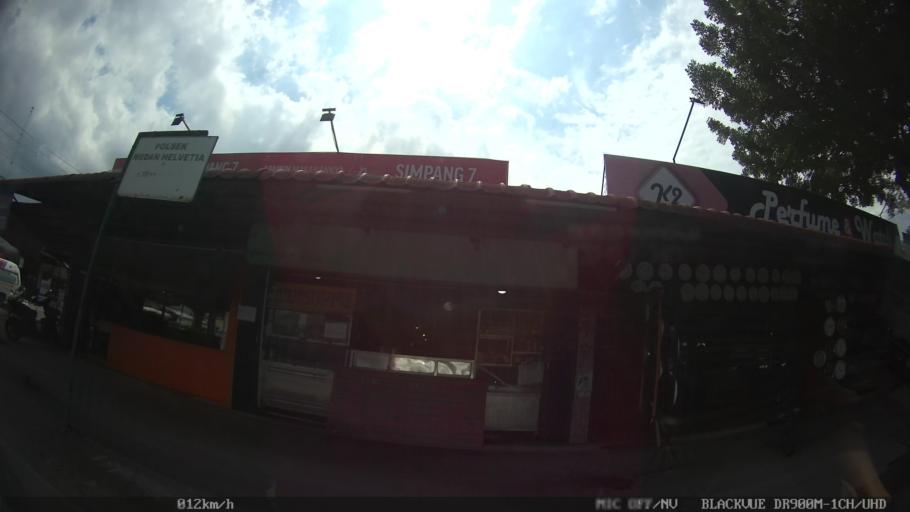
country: ID
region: North Sumatra
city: Medan
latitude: 3.6049
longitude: 98.6447
